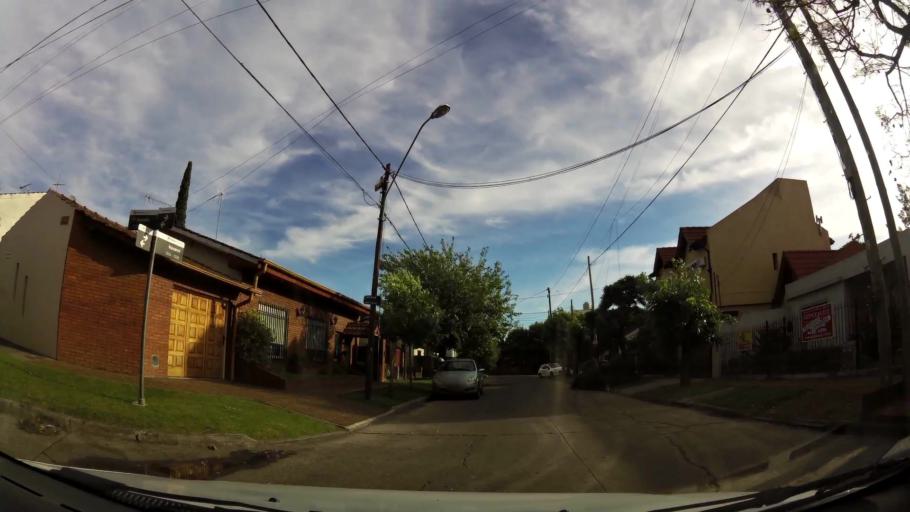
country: AR
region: Buenos Aires
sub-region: Partido de Moron
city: Moron
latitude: -34.6377
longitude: -58.6330
